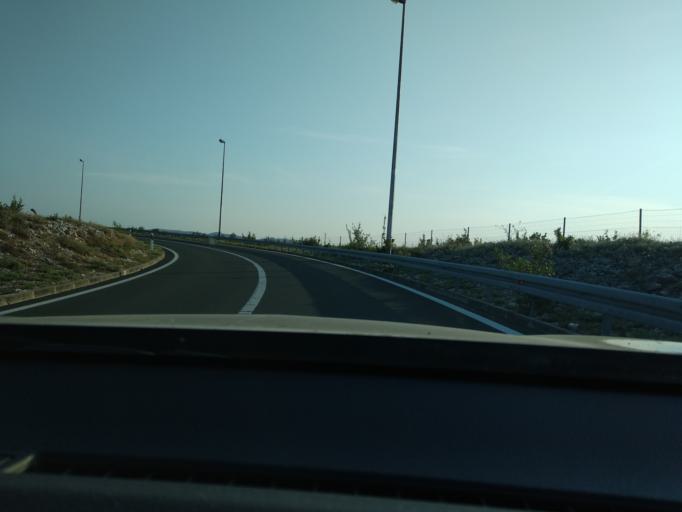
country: HR
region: Sibensko-Kniniska
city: Zaton
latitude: 43.8895
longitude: 15.7905
